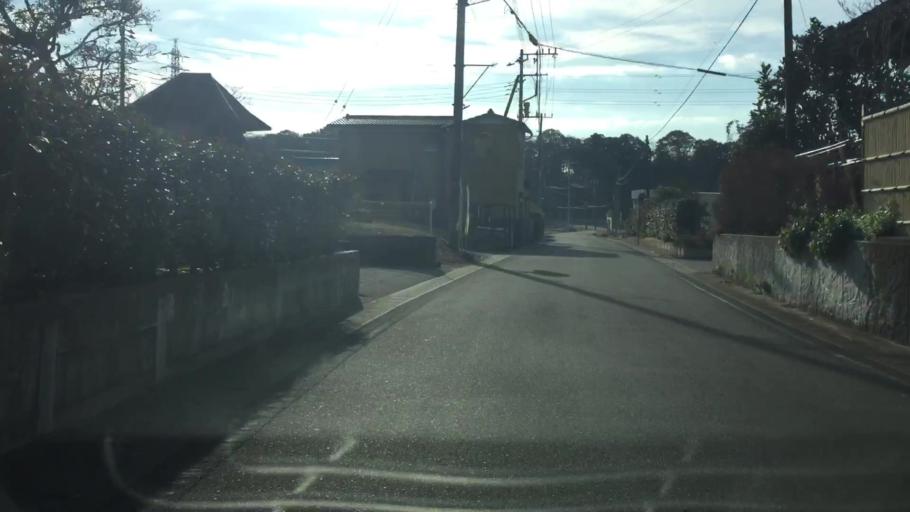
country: JP
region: Chiba
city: Shiroi
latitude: 35.8266
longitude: 140.1211
